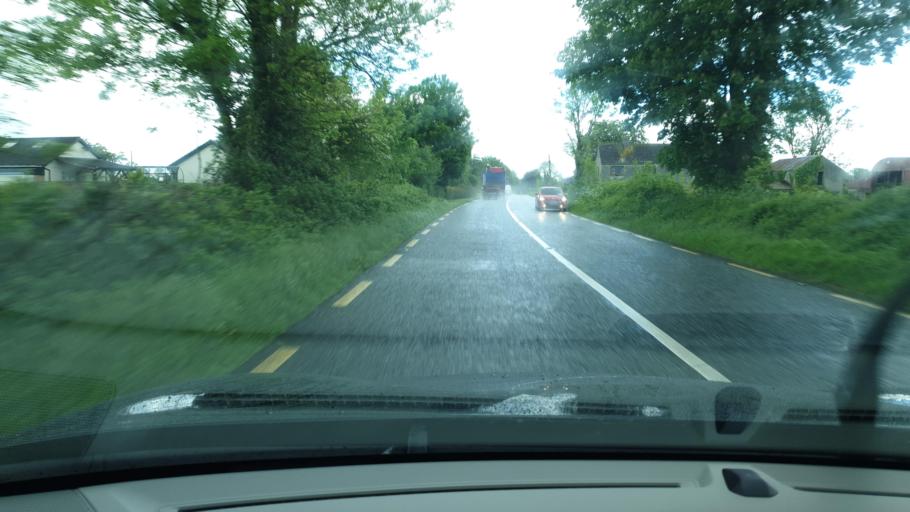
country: IE
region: Leinster
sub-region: Laois
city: Mountmellick
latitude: 53.1497
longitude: -7.3701
